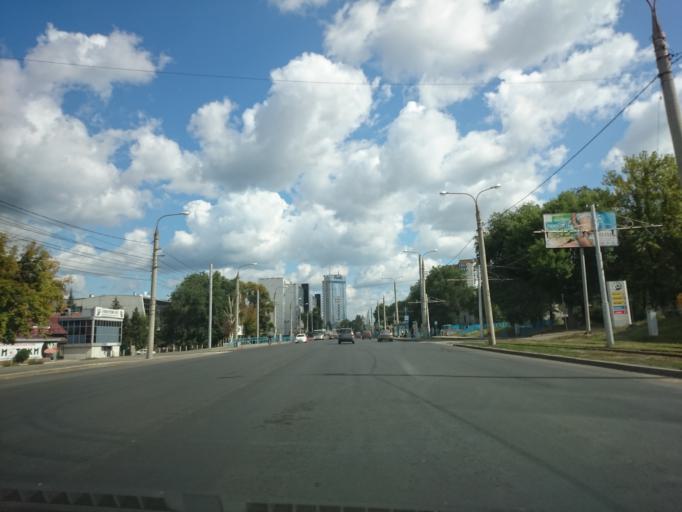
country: RU
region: Samara
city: Samara
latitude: 53.2149
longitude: 50.1455
